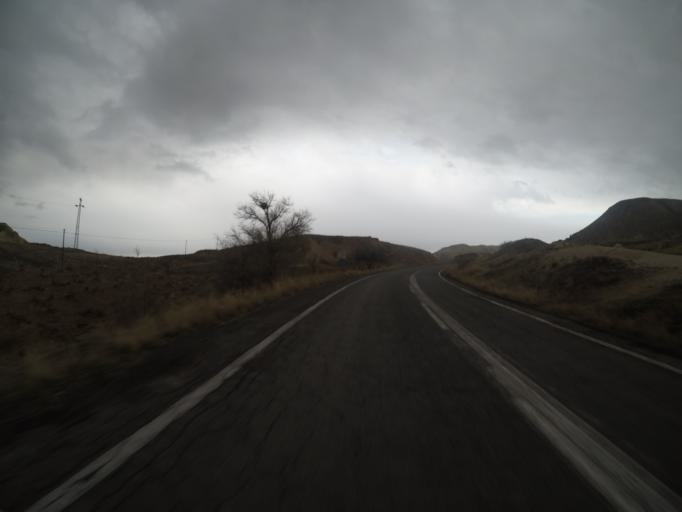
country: TR
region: Nevsehir
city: Avanos
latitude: 38.6794
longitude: 34.8506
